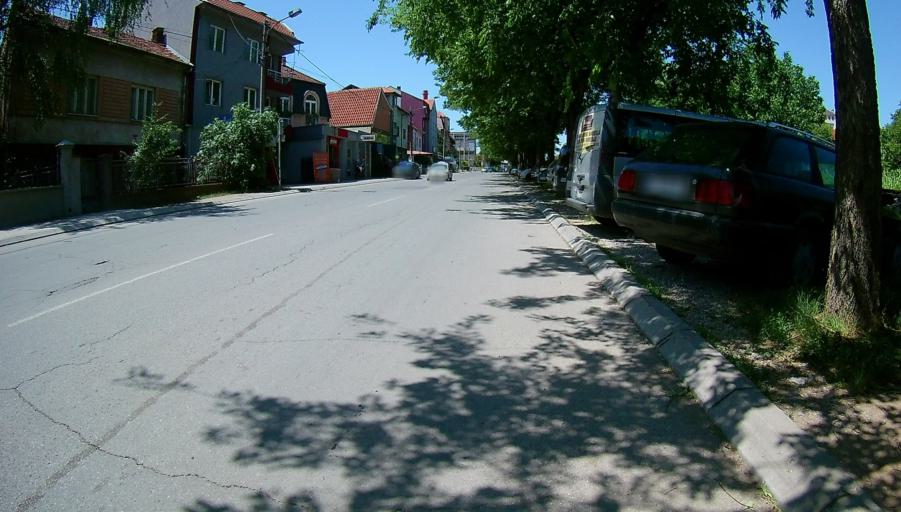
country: RS
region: Central Serbia
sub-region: Nisavski Okrug
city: Nis
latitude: 43.3127
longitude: 21.8958
